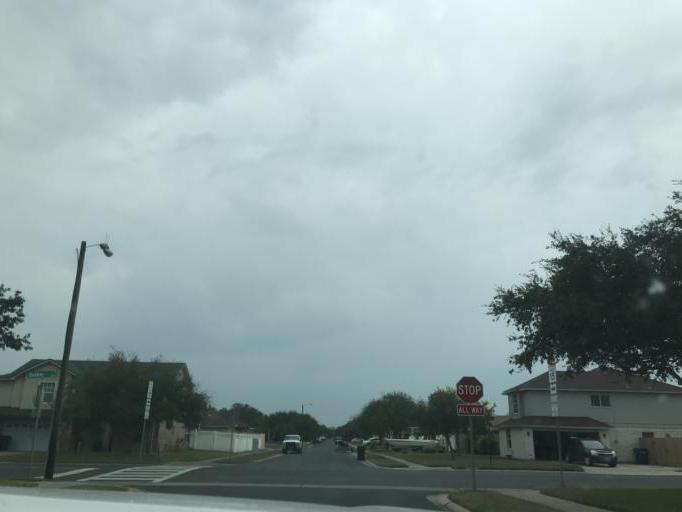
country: US
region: Texas
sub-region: Nueces County
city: Corpus Christi
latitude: 27.6696
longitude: -97.3442
